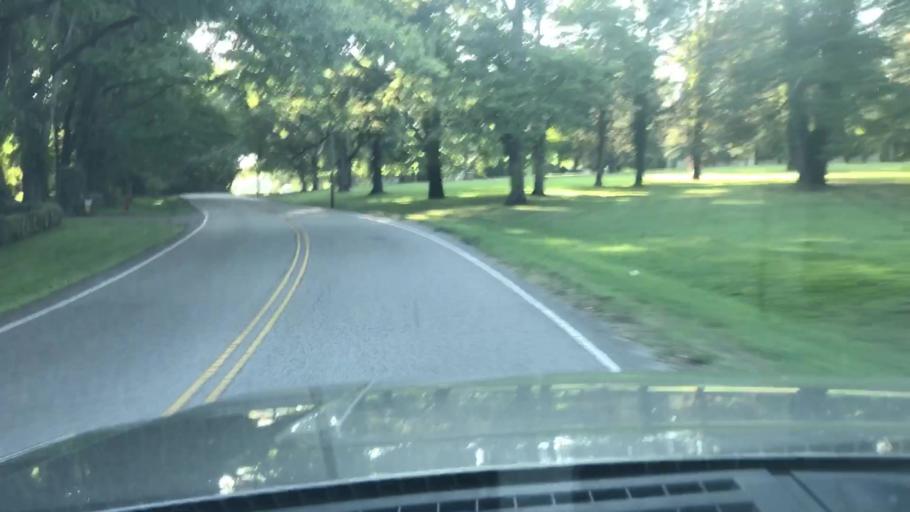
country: US
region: Tennessee
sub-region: Davidson County
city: Belle Meade
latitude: 36.1232
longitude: -86.8547
